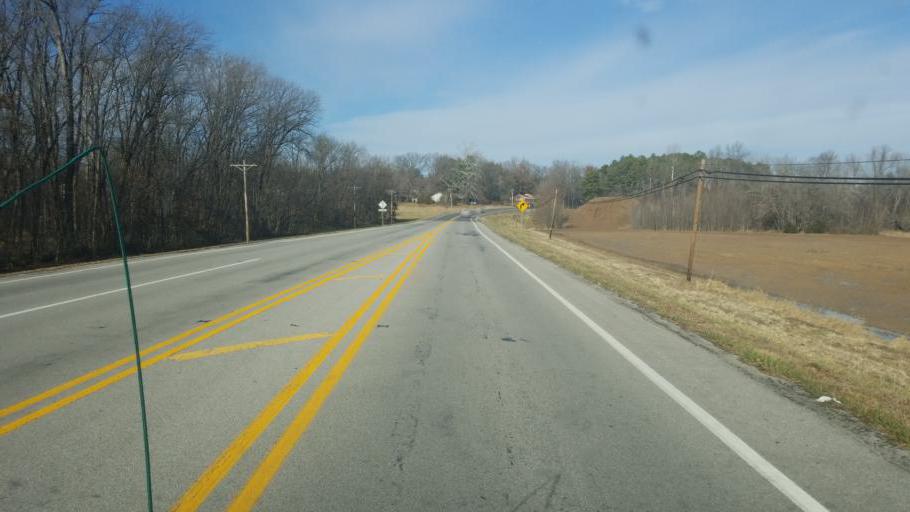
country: US
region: Illinois
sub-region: Jackson County
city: Carbondale
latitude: 37.7017
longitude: -89.1840
